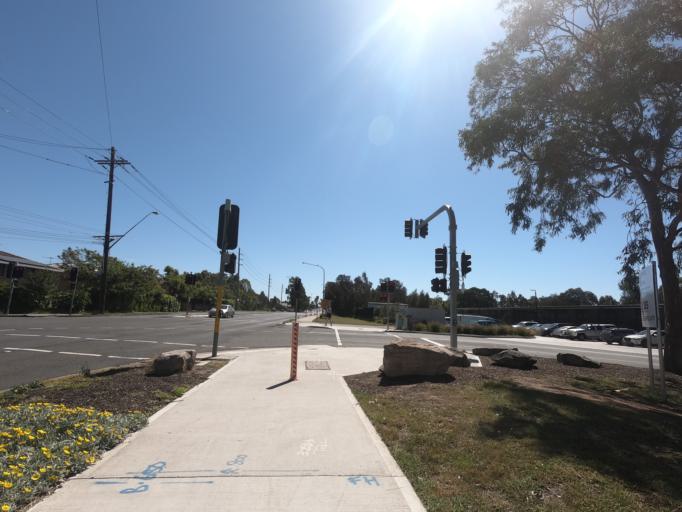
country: AU
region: New South Wales
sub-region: Liverpool
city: Miller
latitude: -33.9280
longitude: 150.9126
